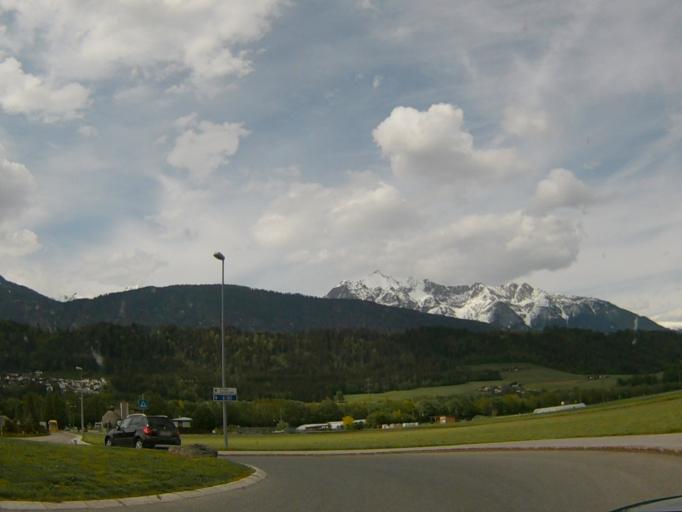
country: AT
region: Tyrol
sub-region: Politischer Bezirk Innsbruck Land
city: Wattenberg
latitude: 47.2957
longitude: 11.6054
